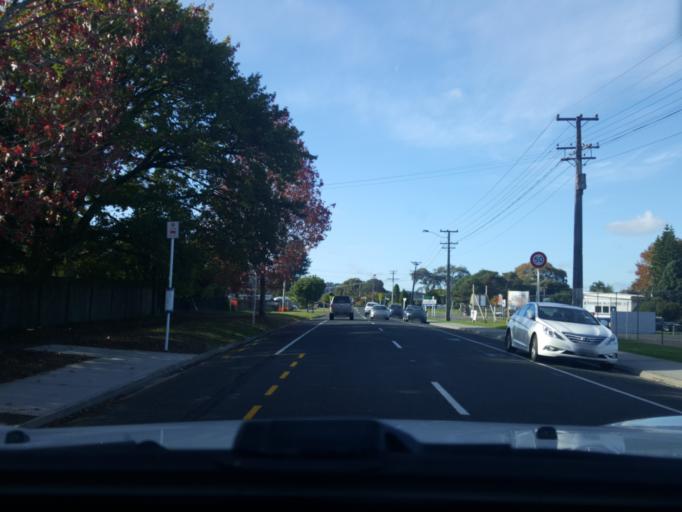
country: NZ
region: Auckland
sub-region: Auckland
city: Rosebank
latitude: -36.7595
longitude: 174.5903
